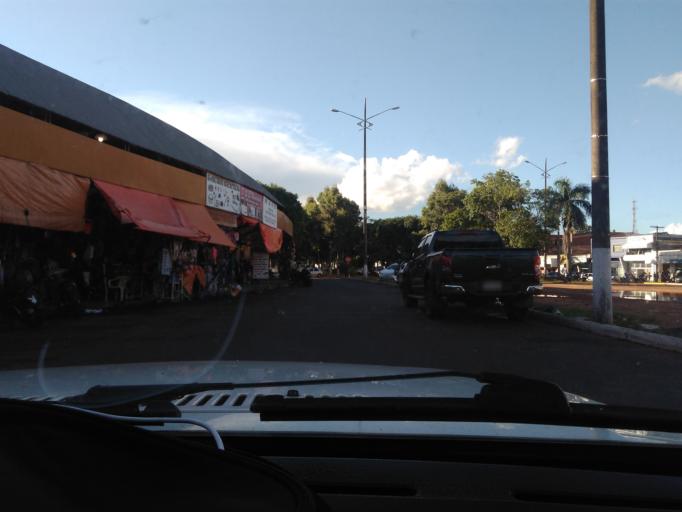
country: BR
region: Mato Grosso do Sul
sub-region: Ponta Pora
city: Ponta Pora
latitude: -22.5367
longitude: -55.7320
